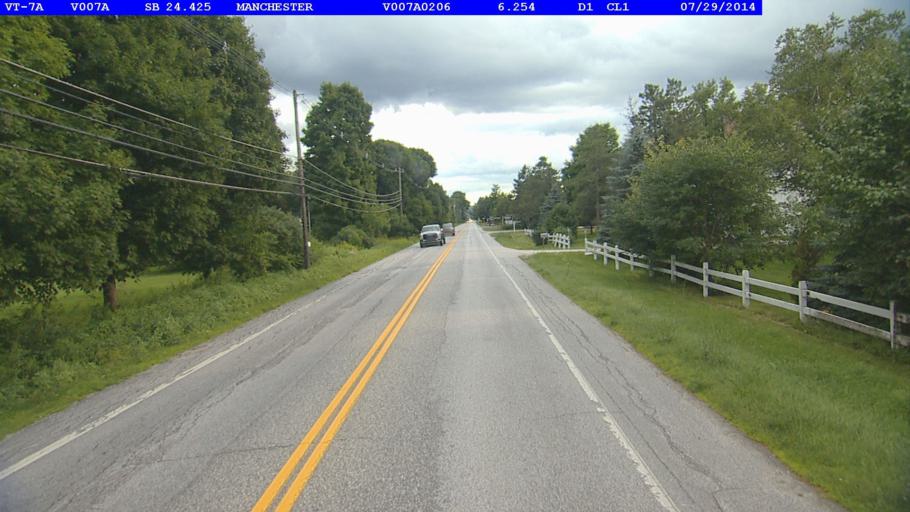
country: US
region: Vermont
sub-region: Bennington County
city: Manchester Center
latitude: 43.1913
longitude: -73.0418
